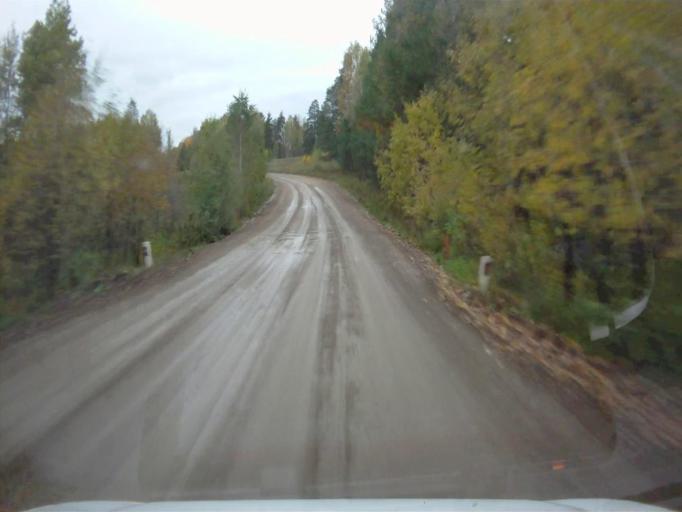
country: RU
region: Chelyabinsk
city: Nyazepetrovsk
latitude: 56.0904
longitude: 59.4137
